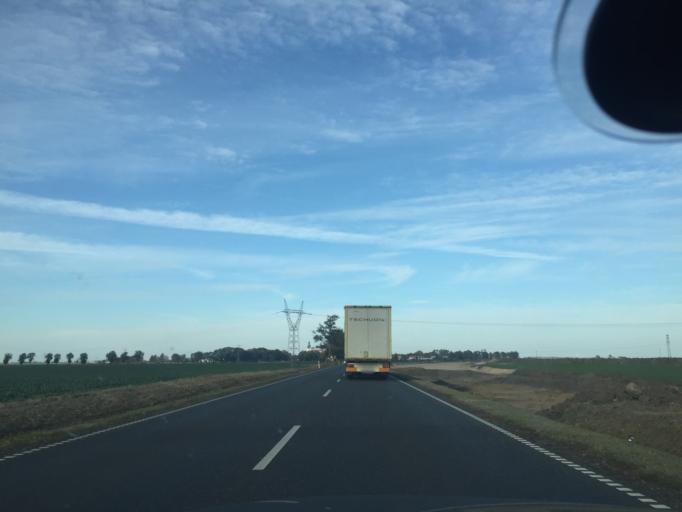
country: PL
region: Kujawsko-Pomorskie
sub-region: Powiat mogilenski
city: Strzelno
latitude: 52.6948
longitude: 18.2100
